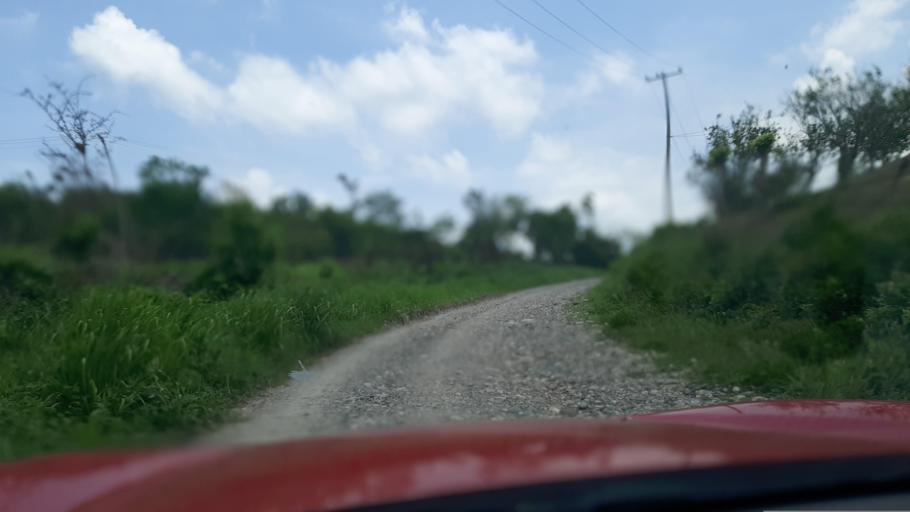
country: MX
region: Veracruz
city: Agua Dulce
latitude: 20.4147
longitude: -97.2781
